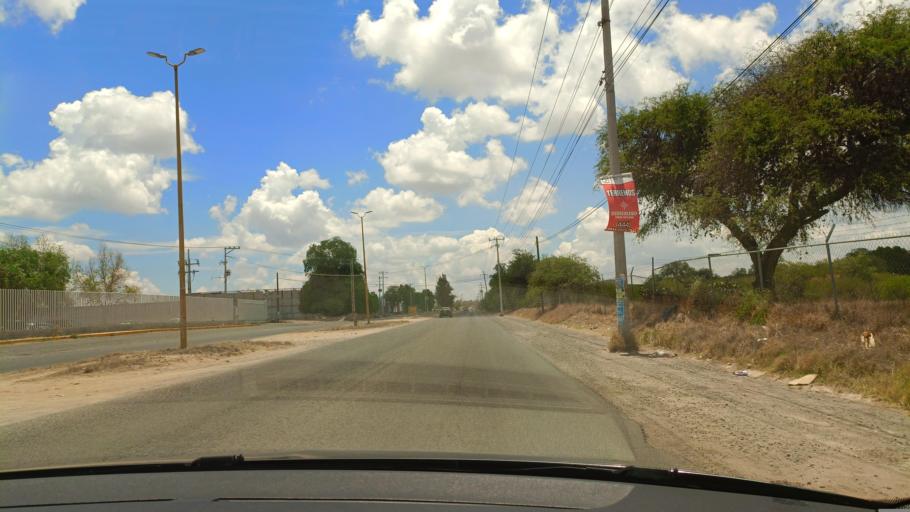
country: MX
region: Guanajuato
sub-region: San Luis de la Paz
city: San Ignacio
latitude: 21.2875
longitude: -100.5405
